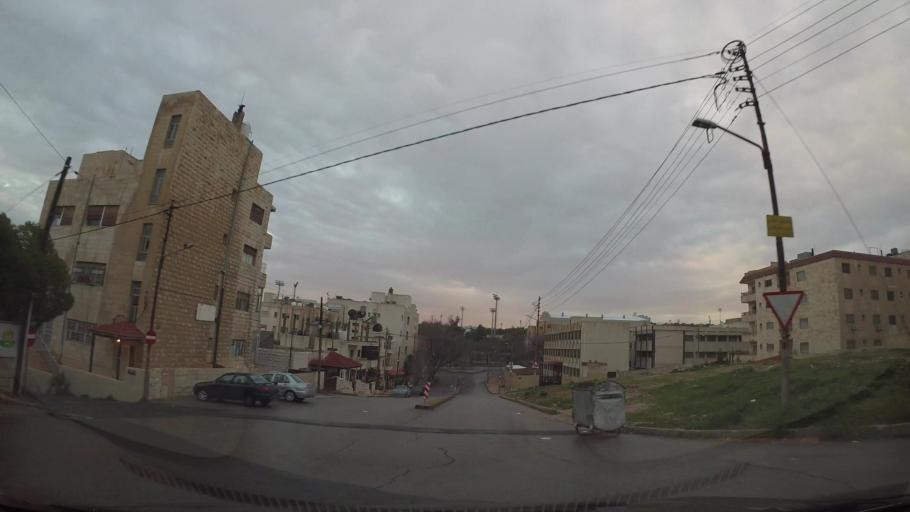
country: JO
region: Amman
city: Amman
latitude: 31.9820
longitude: 35.9121
